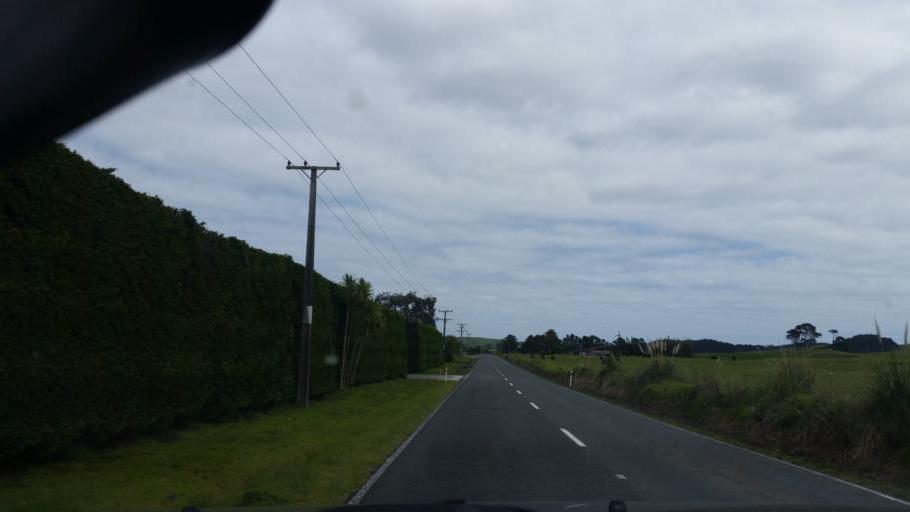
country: NZ
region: Northland
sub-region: Kaipara District
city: Dargaville
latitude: -35.9442
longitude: 173.8220
